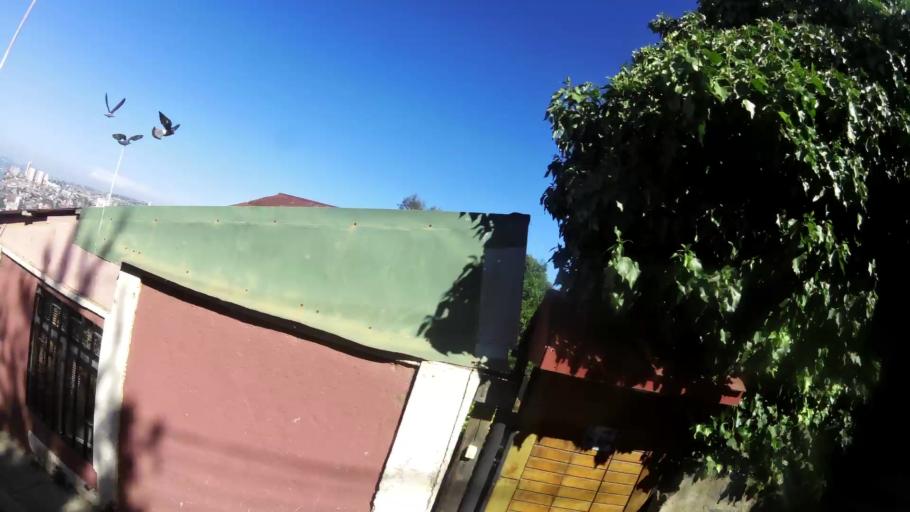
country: CL
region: Valparaiso
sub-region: Provincia de Valparaiso
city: Valparaiso
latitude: -33.0546
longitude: -71.6159
